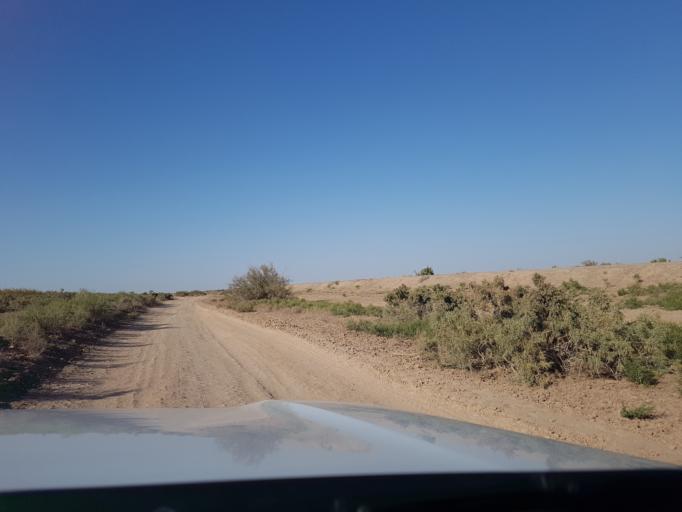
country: IR
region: Razavi Khorasan
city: Sarakhs
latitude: 36.9784
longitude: 61.3854
